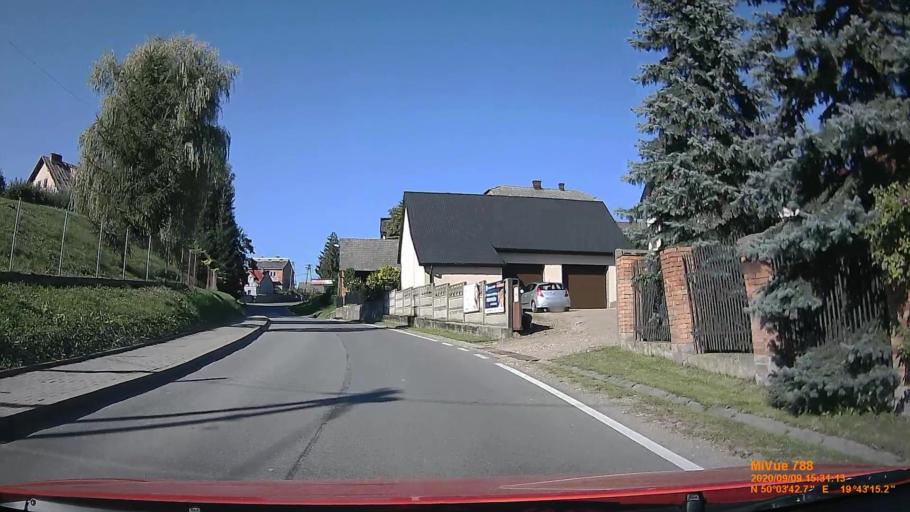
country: PL
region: Lesser Poland Voivodeship
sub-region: Powiat krakowski
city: Mnikow
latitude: 50.0618
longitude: 19.7209
